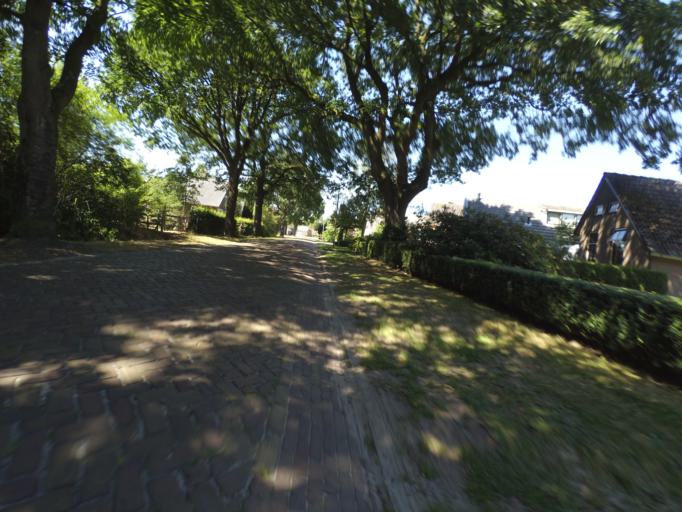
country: NL
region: Drenthe
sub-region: Gemeente Assen
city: Assen
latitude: 52.8840
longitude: 6.6482
